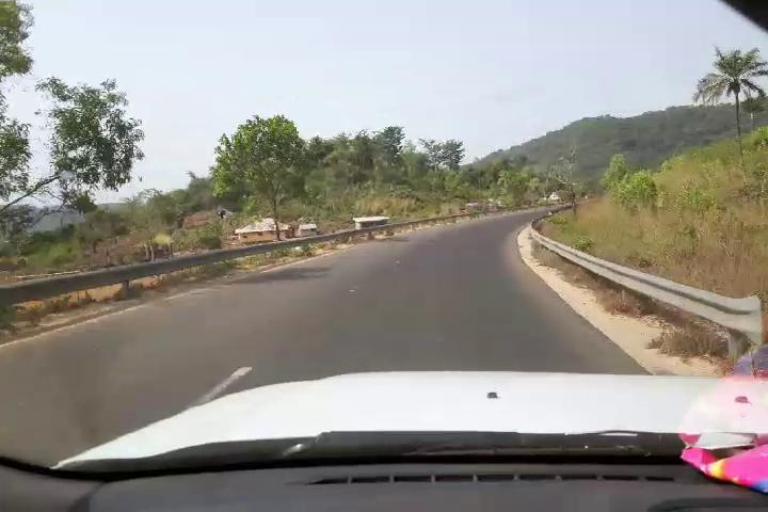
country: SL
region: Western Area
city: Waterloo
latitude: 8.2702
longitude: -13.1588
